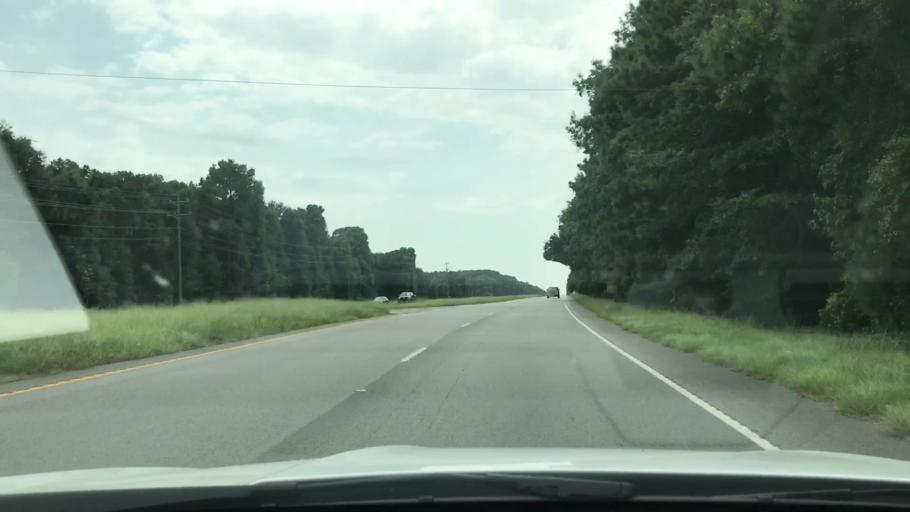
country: US
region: South Carolina
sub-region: Charleston County
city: Isle of Palms
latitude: 32.9179
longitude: -79.7172
